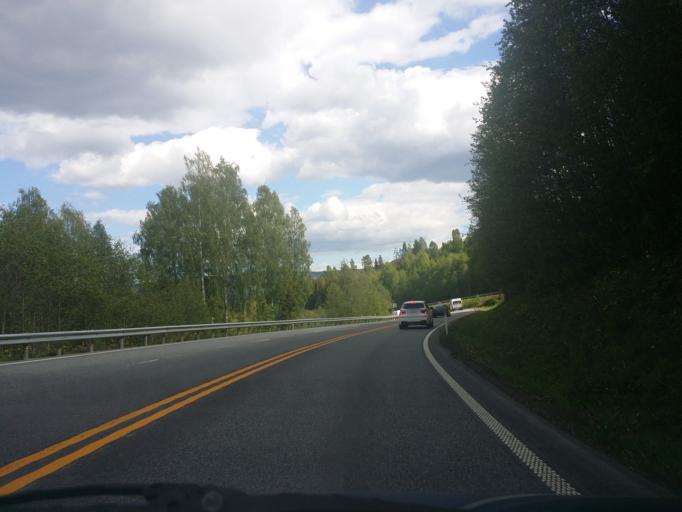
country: NO
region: Oppland
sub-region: Lunner
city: Roa
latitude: 60.2949
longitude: 10.5962
